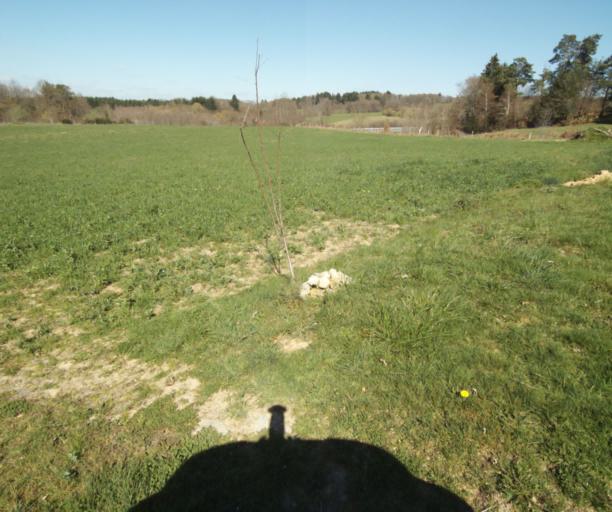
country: FR
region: Limousin
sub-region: Departement de la Correze
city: Saint-Mexant
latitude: 45.3058
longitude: 1.6682
